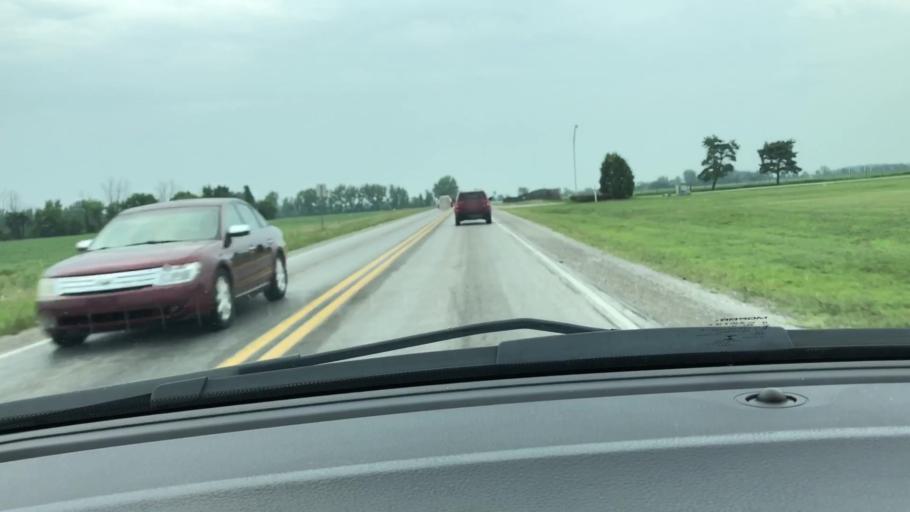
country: US
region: Michigan
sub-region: Saginaw County
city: Freeland
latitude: 43.5331
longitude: -84.0952
